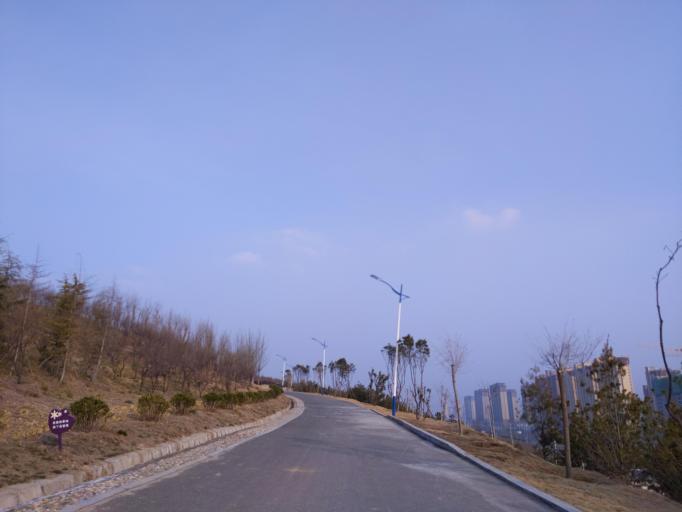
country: CN
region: Henan Sheng
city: Puyang
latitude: 35.8190
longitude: 115.0107
